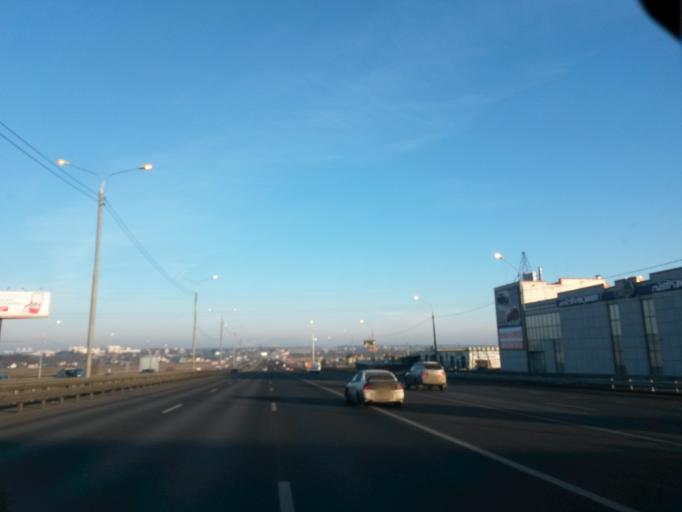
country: RU
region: Moskovskaya
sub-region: Podol'skiy Rayon
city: Podol'sk
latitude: 55.4486
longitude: 37.6177
